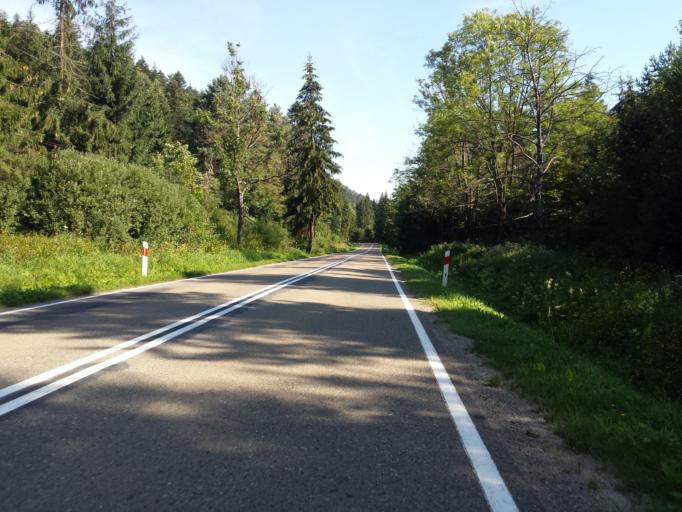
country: PL
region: Subcarpathian Voivodeship
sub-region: Powiat leski
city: Baligrod
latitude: 49.2935
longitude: 22.2683
